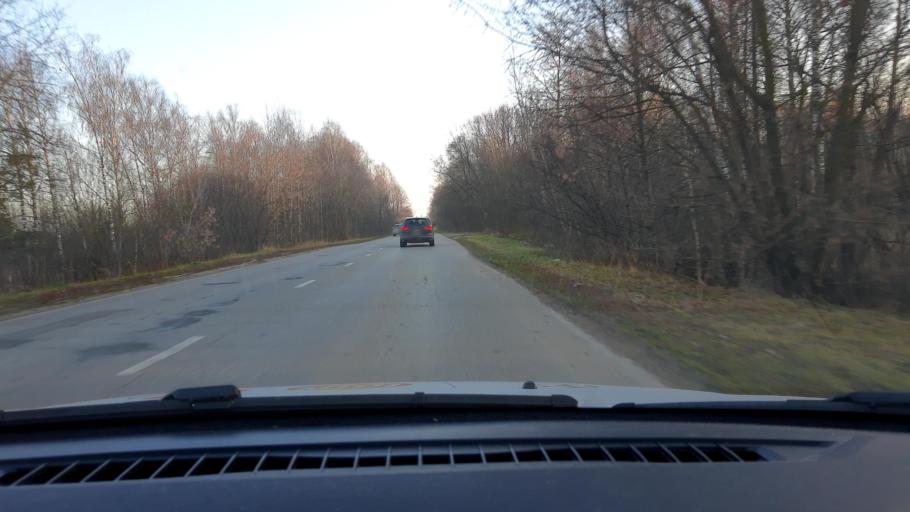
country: RU
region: Nizjnij Novgorod
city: Volodarsk
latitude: 56.2485
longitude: 43.1764
